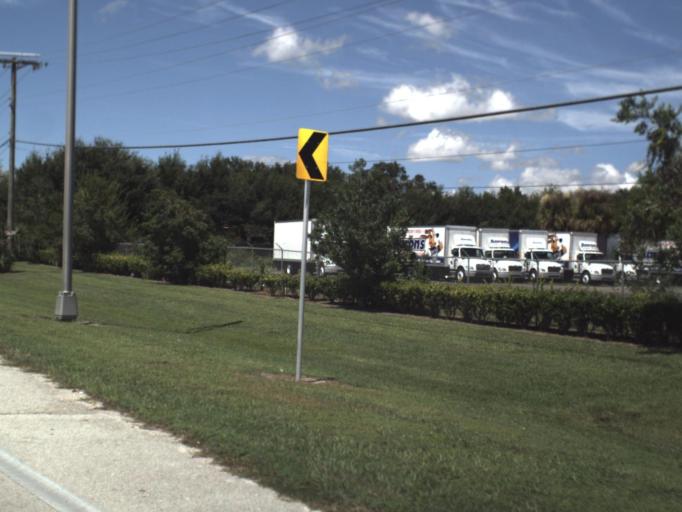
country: US
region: Florida
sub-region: Polk County
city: Auburndale
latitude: 28.0641
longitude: -81.7712
